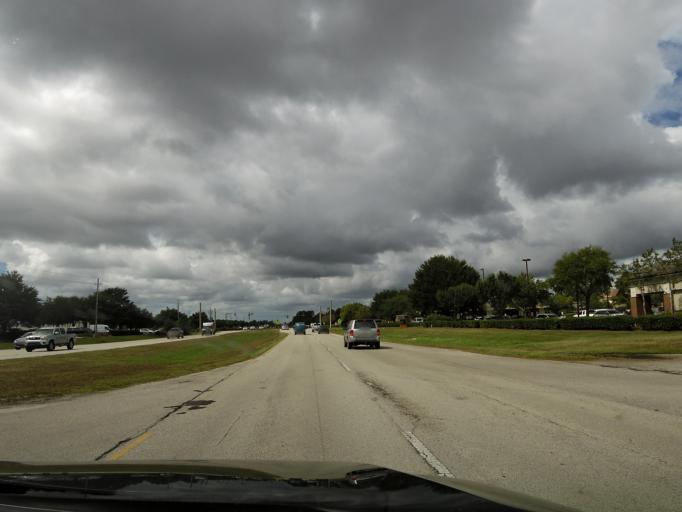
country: US
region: Florida
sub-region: Clay County
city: Orange Park
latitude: 30.1024
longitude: -81.7098
